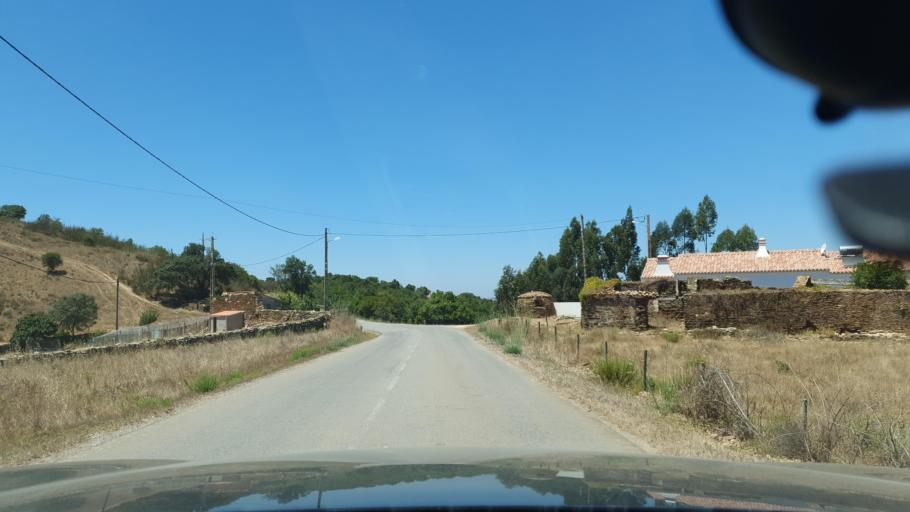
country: PT
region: Beja
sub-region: Odemira
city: Odemira
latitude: 37.5513
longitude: -8.4270
